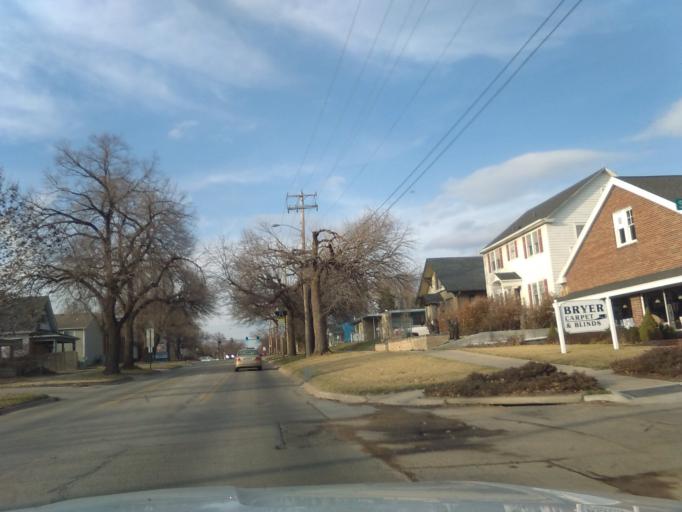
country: US
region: Nebraska
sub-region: Lancaster County
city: Lincoln
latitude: 40.7887
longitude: -96.7028
